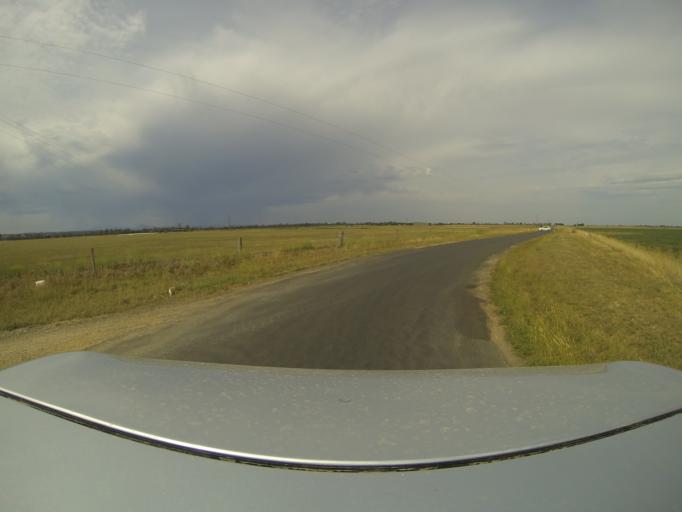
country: AU
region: Victoria
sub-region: Wellington
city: Heyfield
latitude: -37.9987
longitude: 146.6894
